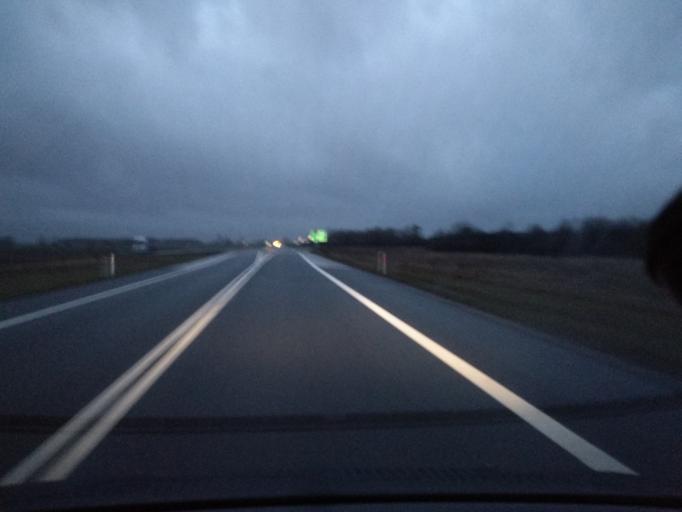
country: PL
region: Lower Silesian Voivodeship
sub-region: Powiat sredzki
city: Miekinia
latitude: 51.1619
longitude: 16.6866
